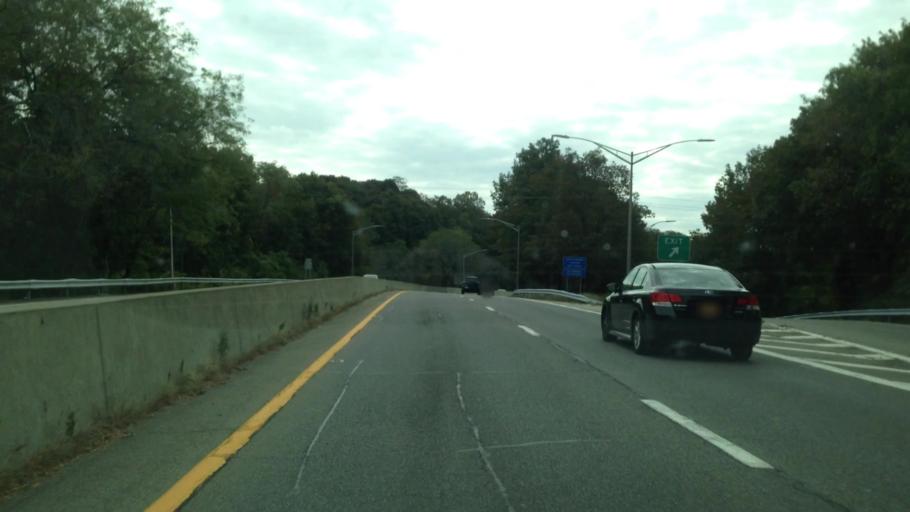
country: US
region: New York
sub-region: Dutchess County
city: Poughkeepsie
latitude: 41.6888
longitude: -73.9327
